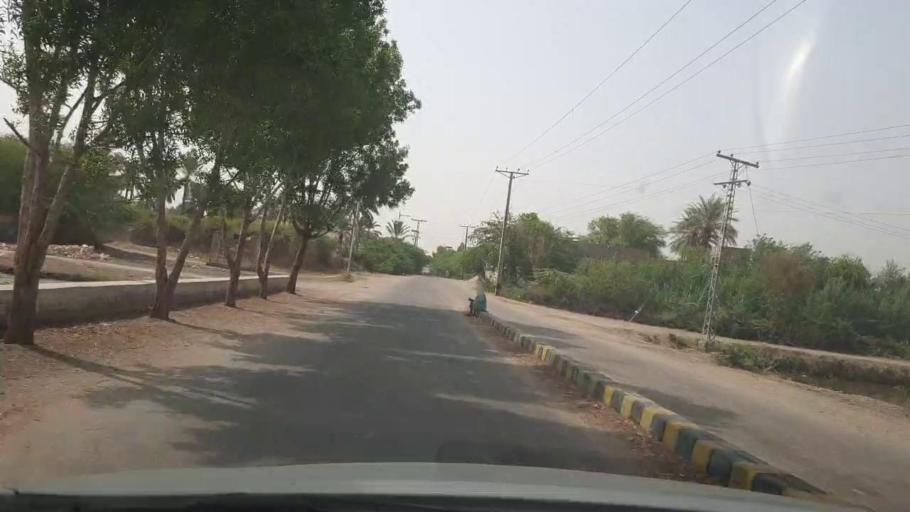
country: PK
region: Sindh
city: Kot Diji
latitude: 27.3500
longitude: 68.7122
